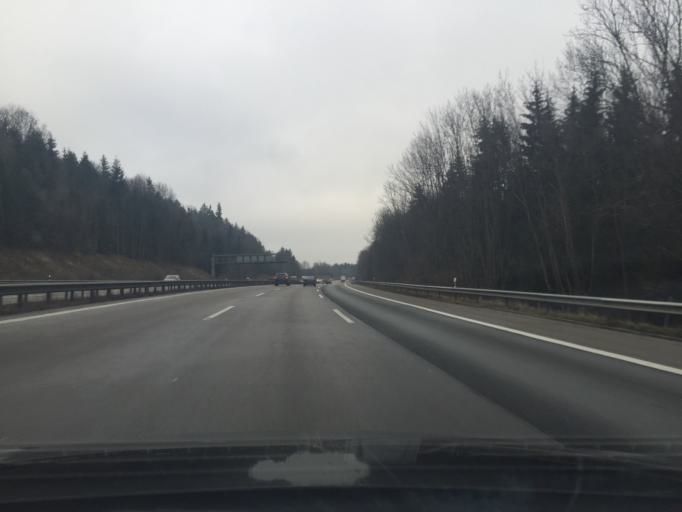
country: DE
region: Bavaria
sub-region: Upper Bavaria
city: Vagen
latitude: 47.8387
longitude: 11.8731
